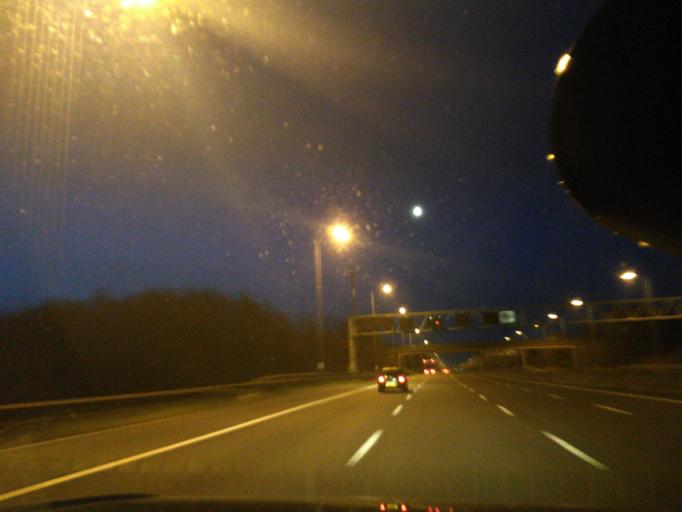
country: GB
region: England
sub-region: Nottinghamshire
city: Hucknall
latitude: 53.0289
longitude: -1.2469
